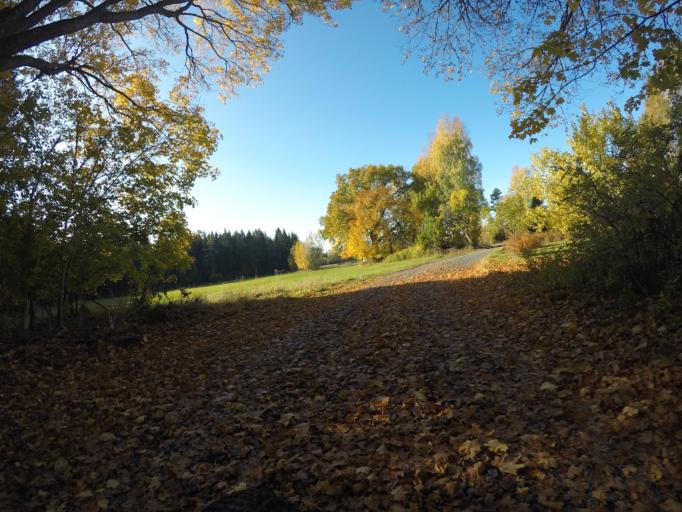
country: SE
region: Vaestmanland
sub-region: Kungsors Kommun
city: Kungsoer
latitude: 59.3277
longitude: 16.1079
